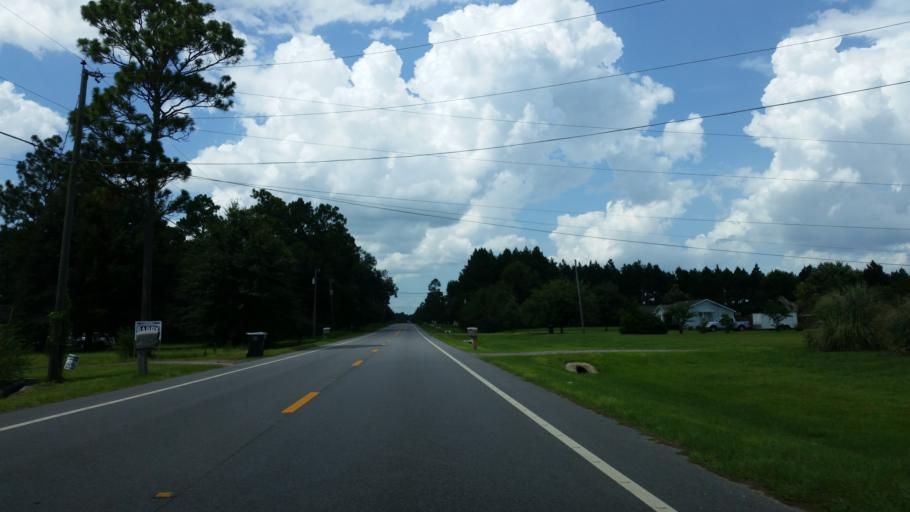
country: US
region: Florida
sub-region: Escambia County
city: Cantonment
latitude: 30.6490
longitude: -87.3857
